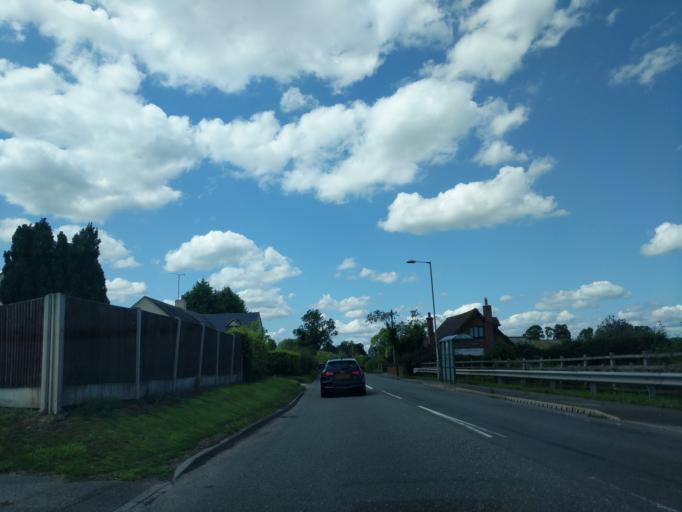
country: GB
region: England
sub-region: Staffordshire
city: Uttoxeter
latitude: 52.9193
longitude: -1.9024
